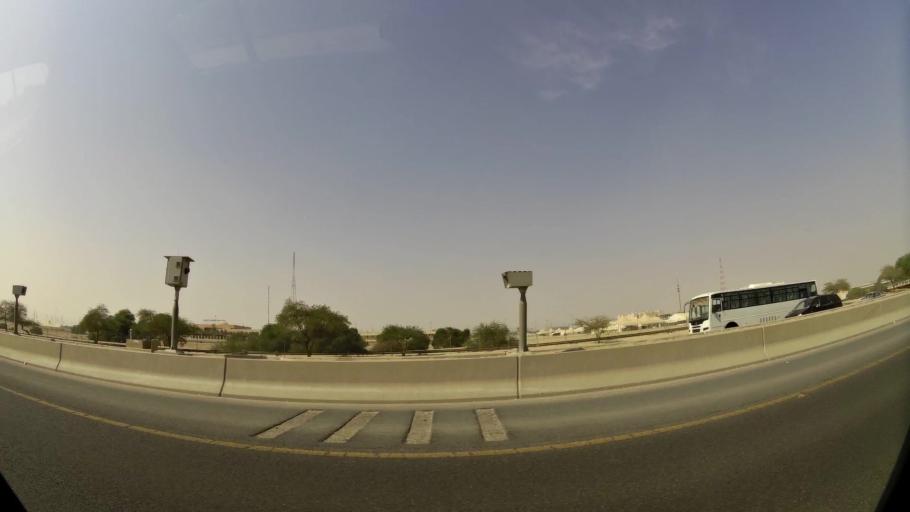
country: KW
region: Al Ahmadi
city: Al Fahahil
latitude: 29.0817
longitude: 48.1141
